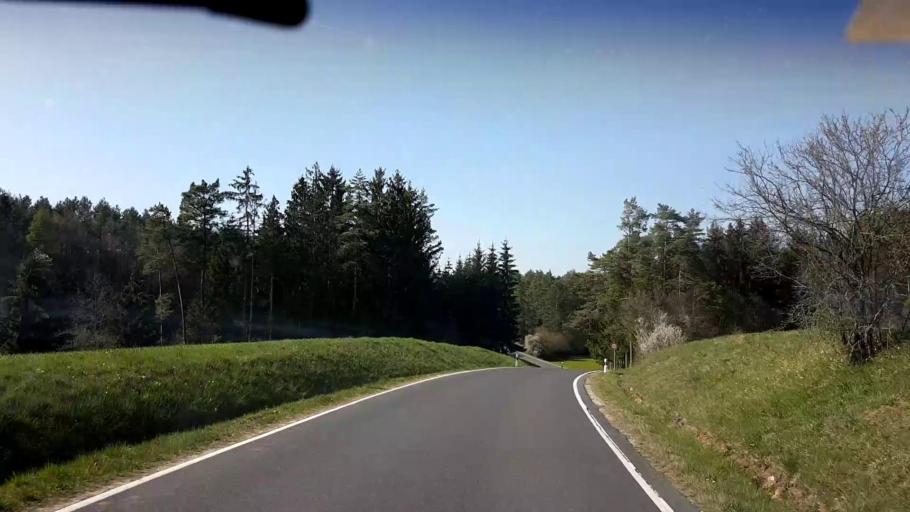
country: DE
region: Bavaria
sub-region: Upper Franconia
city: Waischenfeld
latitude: 49.8053
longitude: 11.3707
